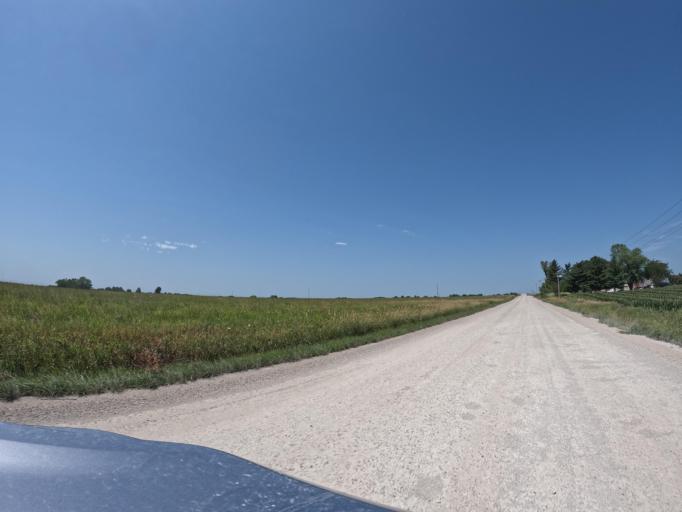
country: US
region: Iowa
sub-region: Henry County
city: Mount Pleasant
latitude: 40.9376
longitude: -91.5230
